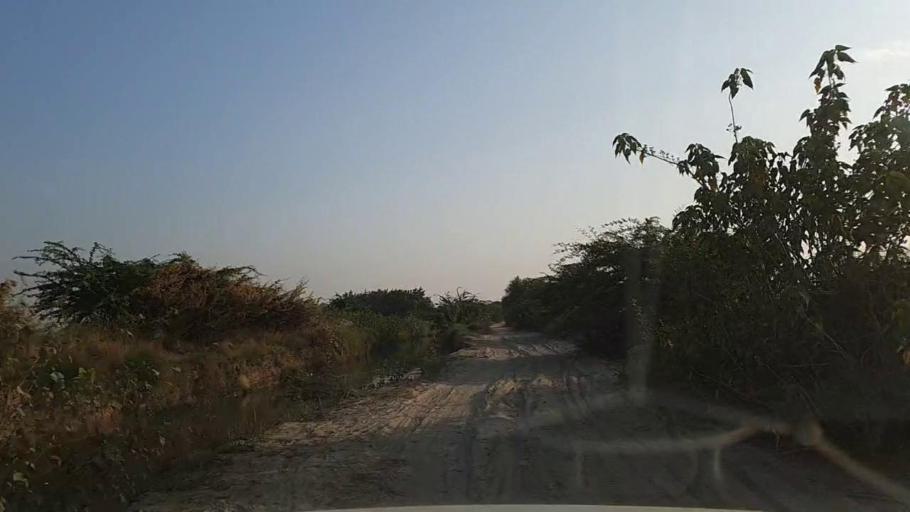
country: PK
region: Sindh
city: Daro Mehar
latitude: 24.7750
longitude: 68.1935
